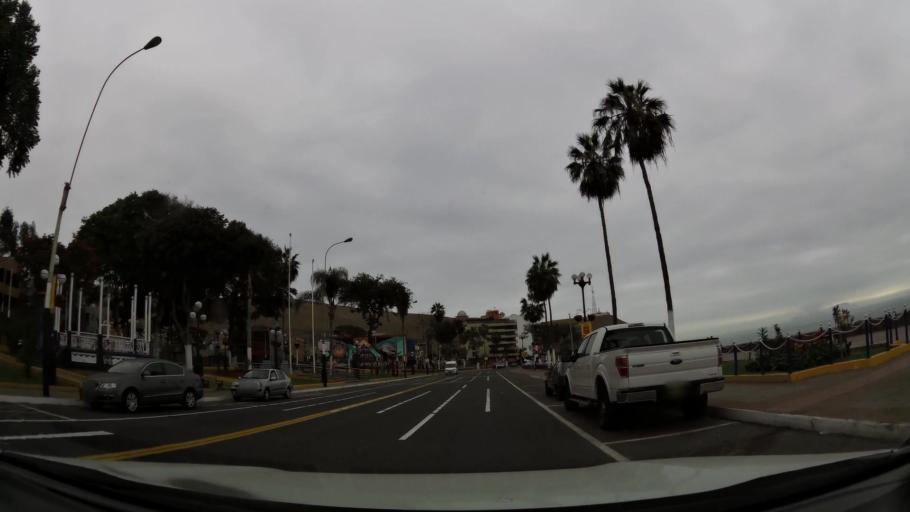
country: PE
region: Lima
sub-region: Lima
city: Surco
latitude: -12.1670
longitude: -77.0286
